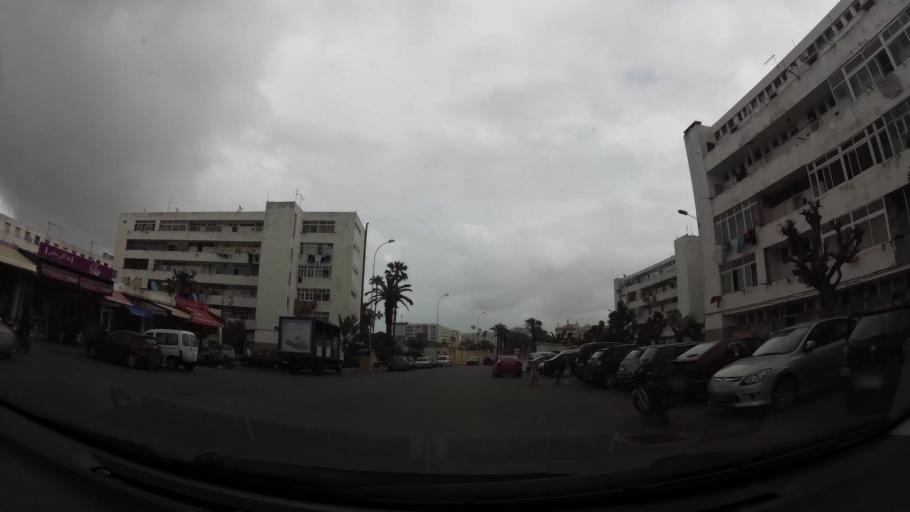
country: MA
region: Grand Casablanca
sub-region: Casablanca
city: Casablanca
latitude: 33.6038
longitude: -7.6508
